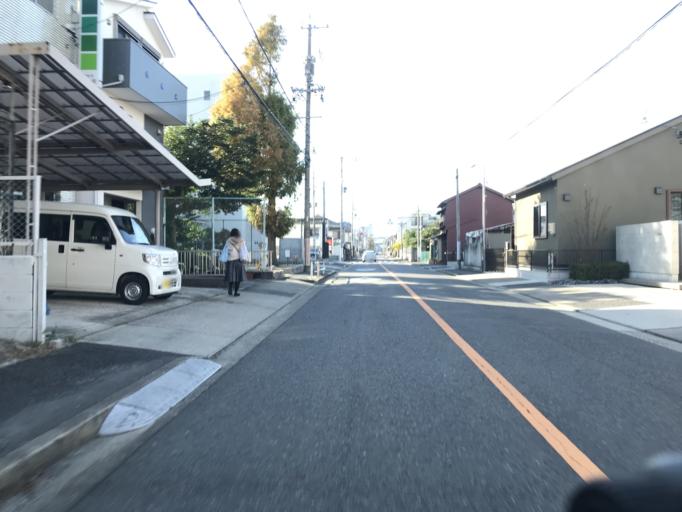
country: JP
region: Aichi
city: Nagoya-shi
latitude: 35.1895
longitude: 136.9219
